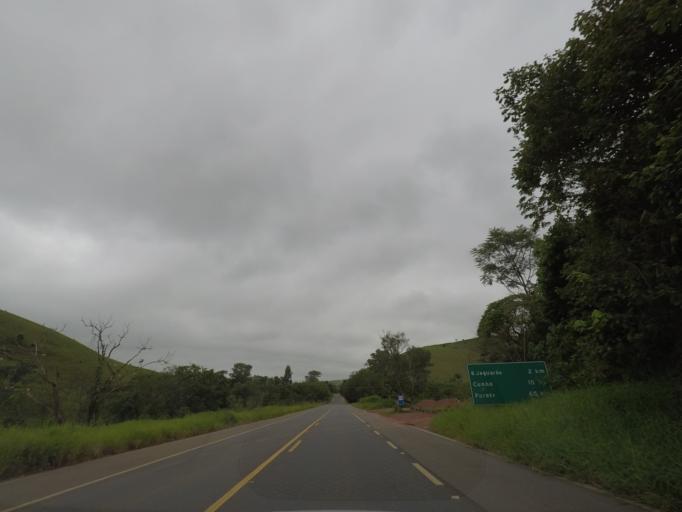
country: BR
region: Sao Paulo
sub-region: Cunha
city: Cunha
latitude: -22.9842
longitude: -45.0436
